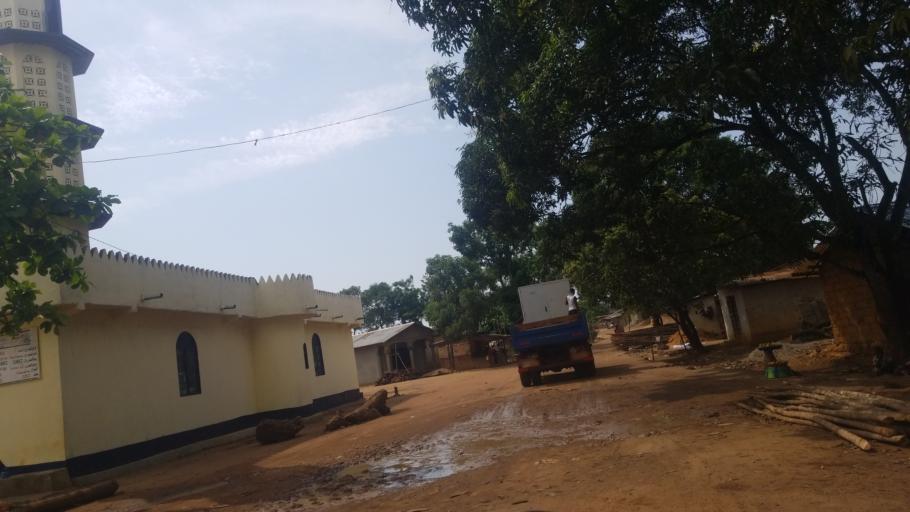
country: SL
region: Western Area
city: Waterloo
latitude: 8.3407
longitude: -13.0480
